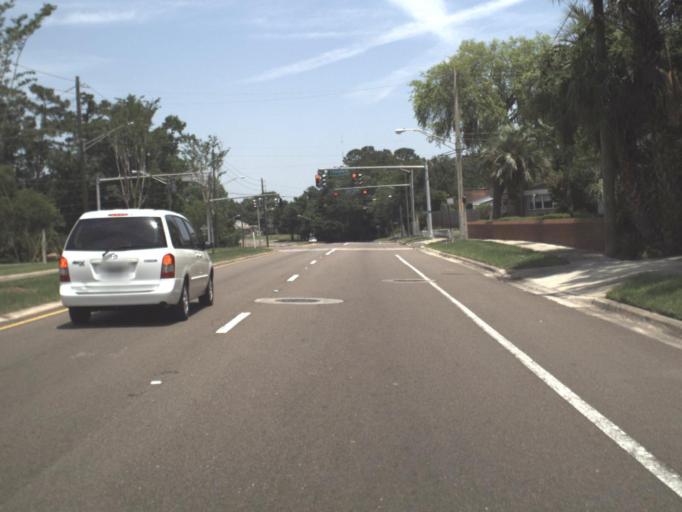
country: US
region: Florida
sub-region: Duval County
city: Jacksonville
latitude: 30.2937
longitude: -81.6480
